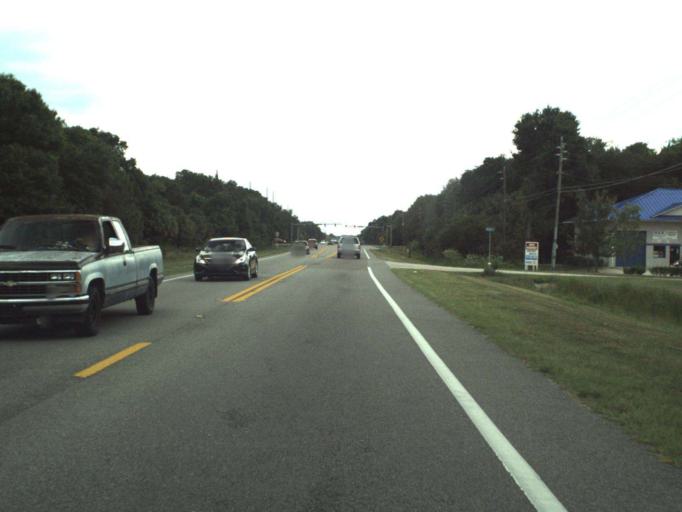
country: US
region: Florida
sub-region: Brevard County
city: Titusville
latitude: 28.5772
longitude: -80.8471
